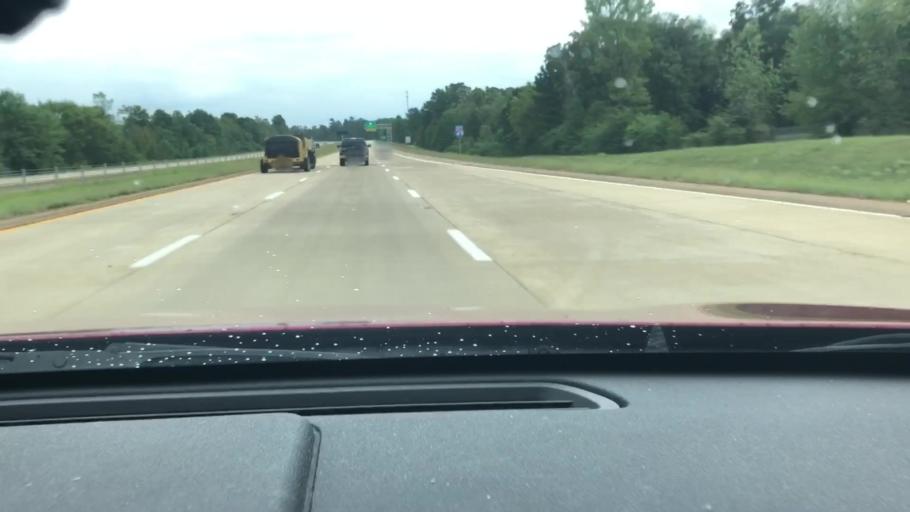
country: US
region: Texas
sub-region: Bowie County
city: Texarkana
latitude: 33.3980
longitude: -94.0099
